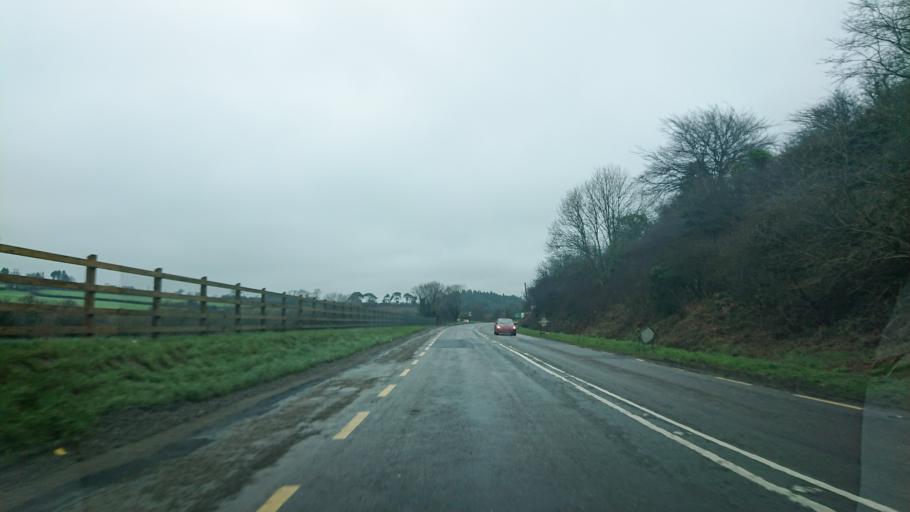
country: IE
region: Munster
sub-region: County Cork
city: Bandon
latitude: 51.7535
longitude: -8.7163
